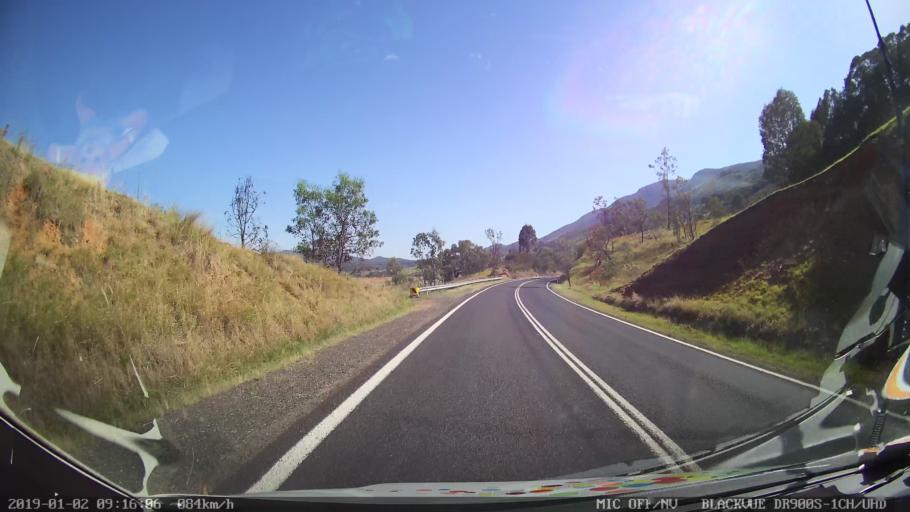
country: AU
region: New South Wales
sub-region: Tumut Shire
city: Tumut
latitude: -35.4569
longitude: 148.2819
